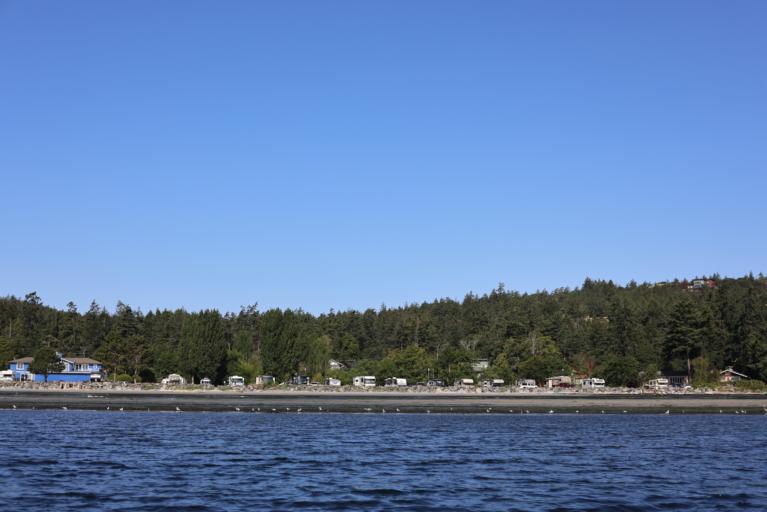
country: CA
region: British Columbia
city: Metchosin
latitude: 48.3525
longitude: -123.5414
